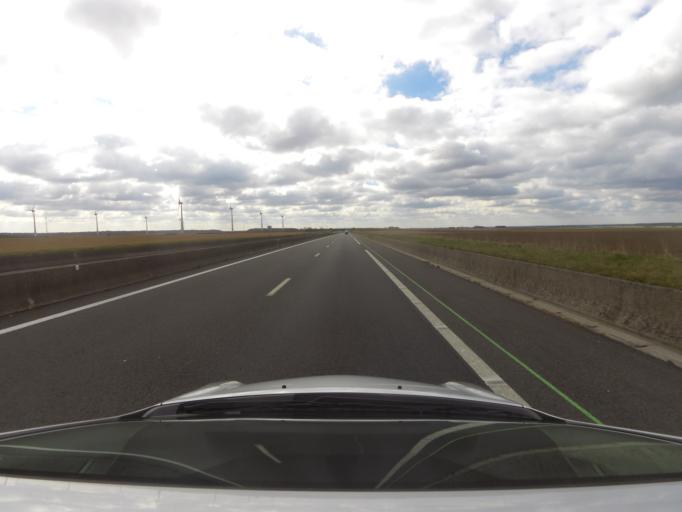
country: FR
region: Picardie
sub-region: Departement de la Somme
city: Rue
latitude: 50.3138
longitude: 1.7223
